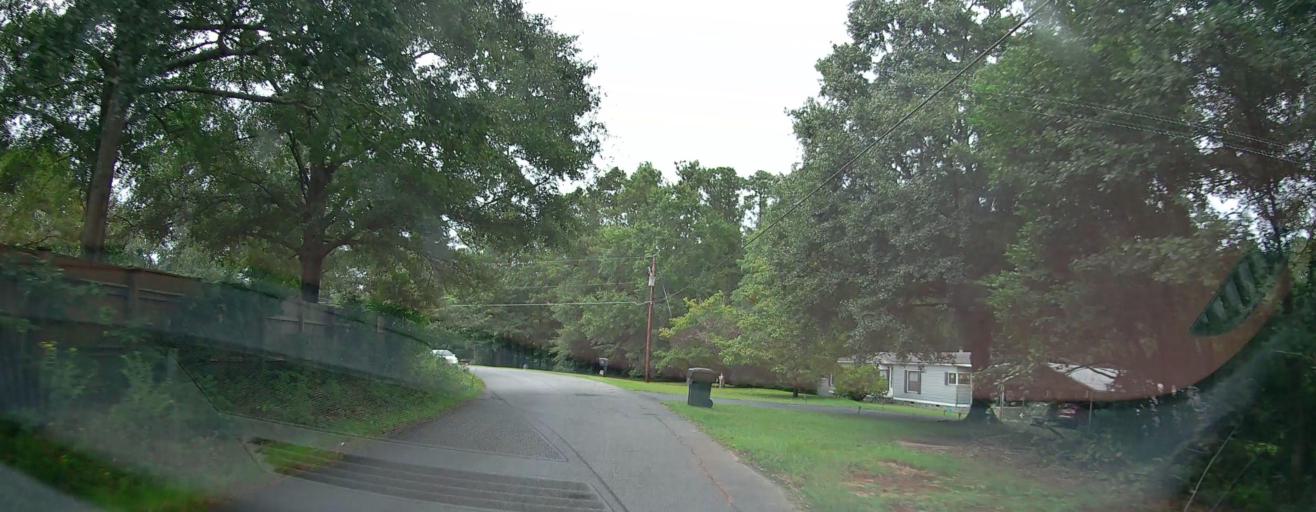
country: US
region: Georgia
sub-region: Peach County
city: Byron
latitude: 32.6773
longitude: -83.7134
